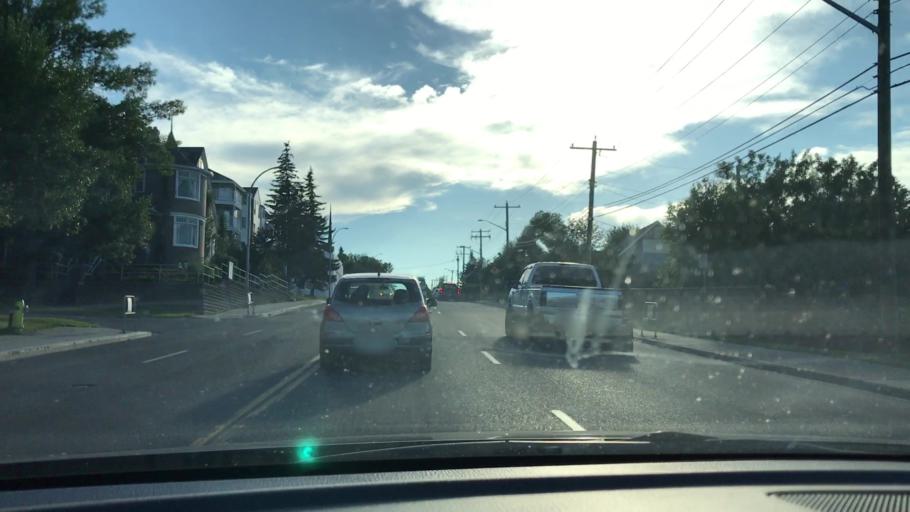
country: CA
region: Alberta
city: Calgary
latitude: 51.0378
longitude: -114.1038
